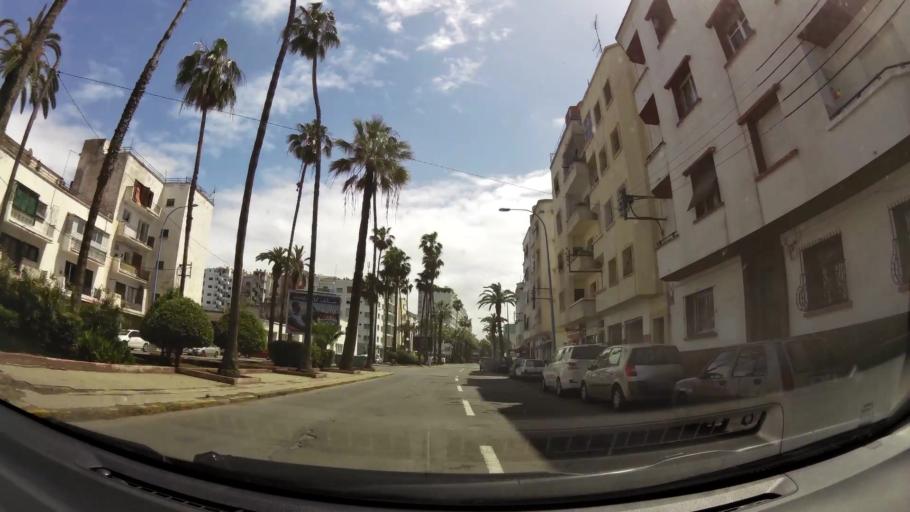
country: MA
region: Grand Casablanca
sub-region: Casablanca
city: Casablanca
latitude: 33.5979
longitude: -7.6318
